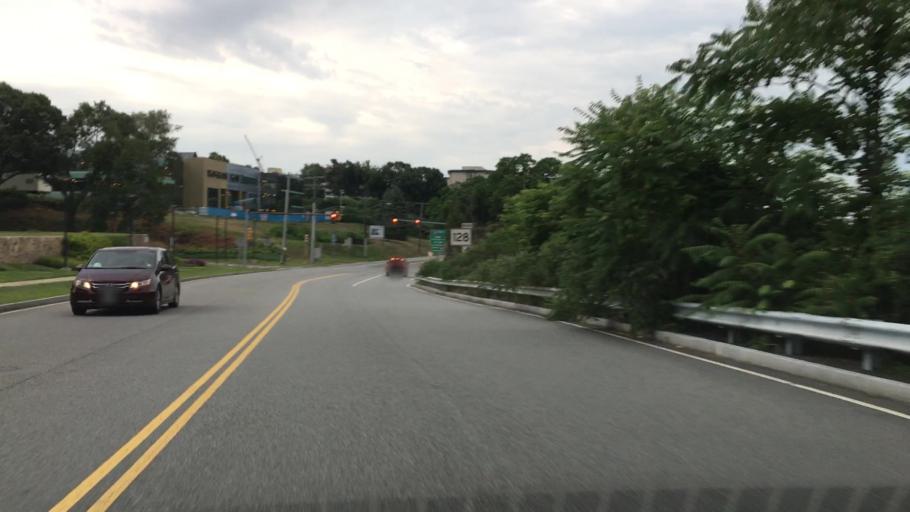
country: US
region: Massachusetts
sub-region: Middlesex County
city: Waltham
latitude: 42.4017
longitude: -71.2589
